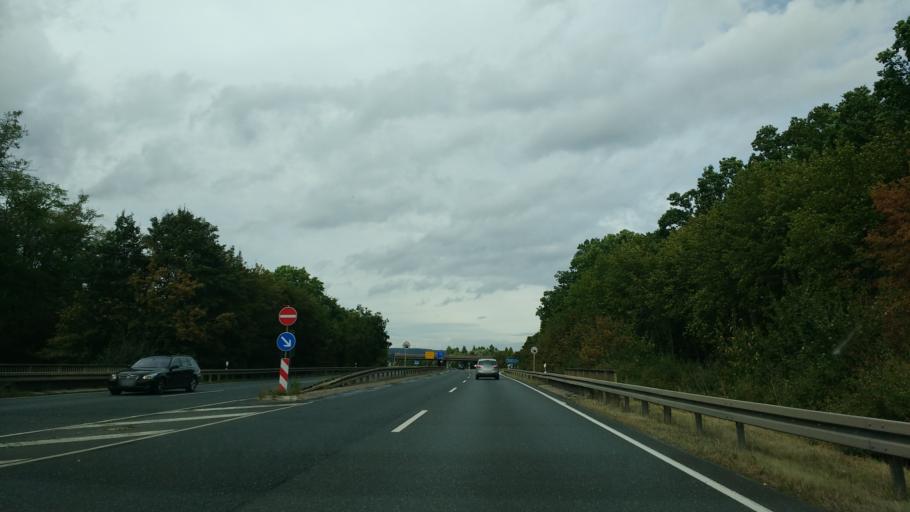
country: DE
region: Bavaria
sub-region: Regierungsbezirk Unterfranken
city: Sennfeld
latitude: 50.0210
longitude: 10.2383
